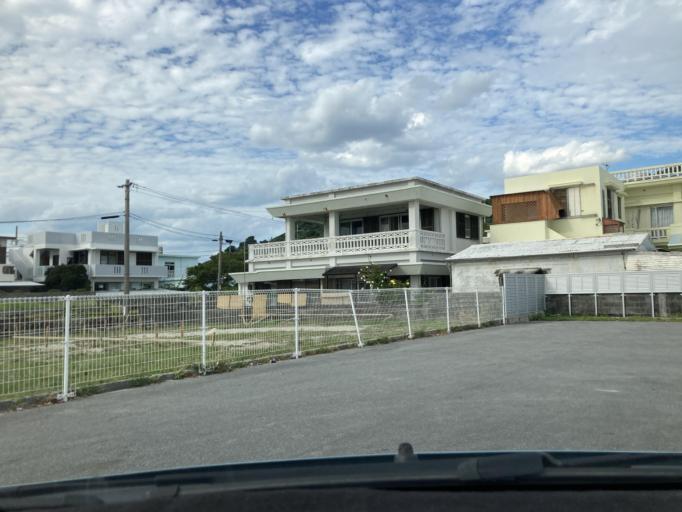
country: JP
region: Okinawa
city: Katsuren-haebaru
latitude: 26.3406
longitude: 127.9546
